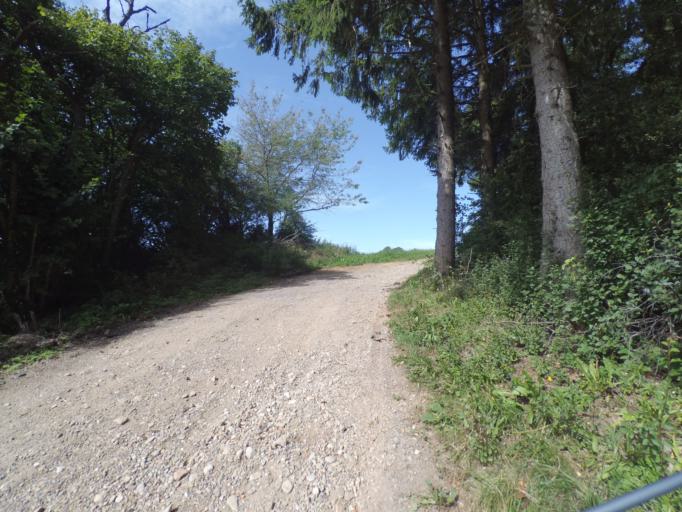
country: DE
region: Baden-Wuerttemberg
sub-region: Freiburg Region
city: Loffingen
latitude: 47.8572
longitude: 8.3304
